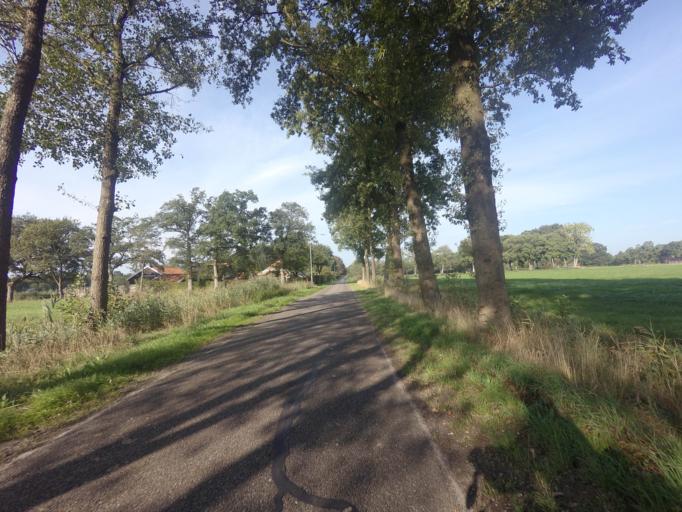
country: NL
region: Groningen
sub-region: Gemeente Leek
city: Leek
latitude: 53.1387
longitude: 6.4781
